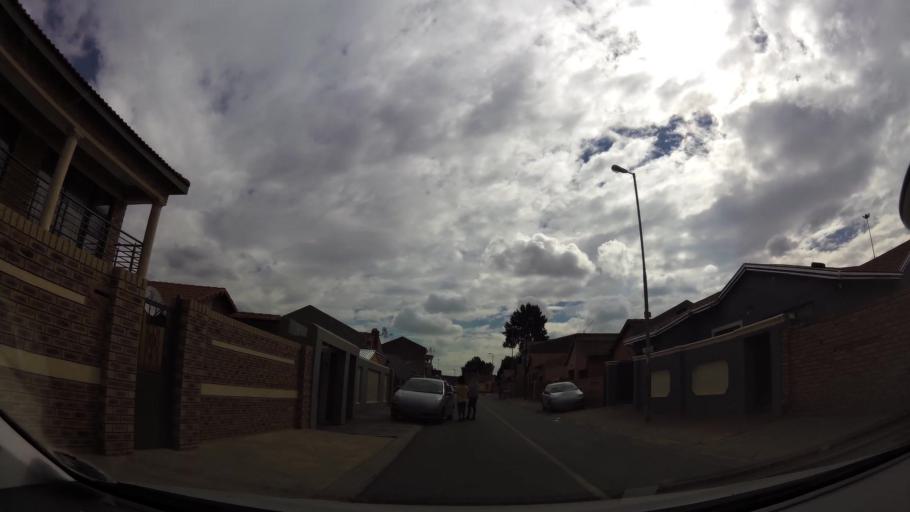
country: ZA
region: Gauteng
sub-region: City of Johannesburg Metropolitan Municipality
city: Soweto
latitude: -26.2829
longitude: 27.8553
